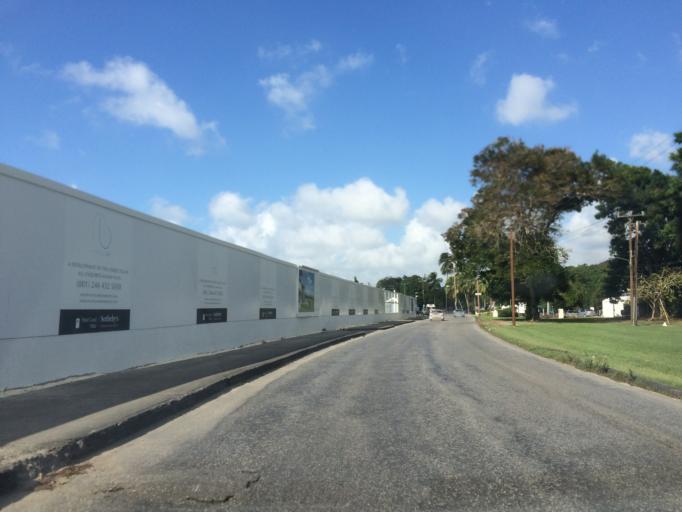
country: BB
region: Saint James
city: Holetown
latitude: 13.1811
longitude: -59.6389
